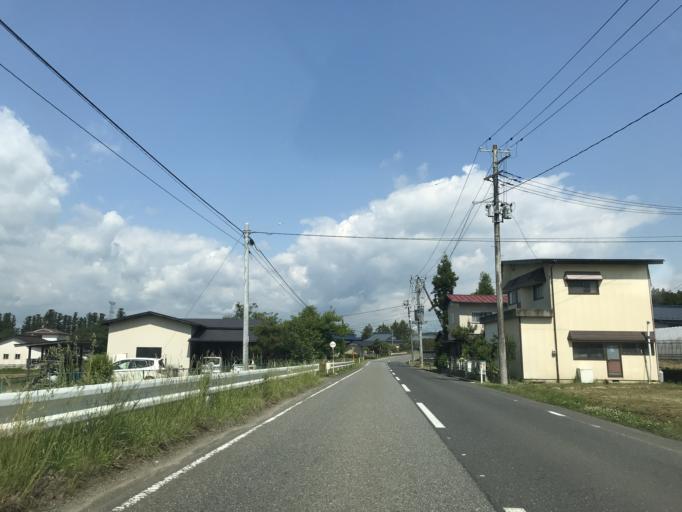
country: JP
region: Iwate
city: Ichinoseki
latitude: 38.7977
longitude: 141.0181
